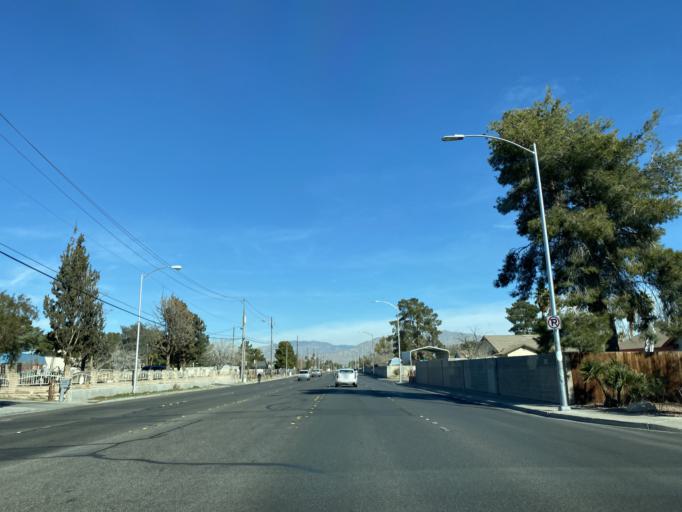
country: US
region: Nevada
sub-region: Clark County
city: Las Vegas
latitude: 36.2194
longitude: -115.2257
